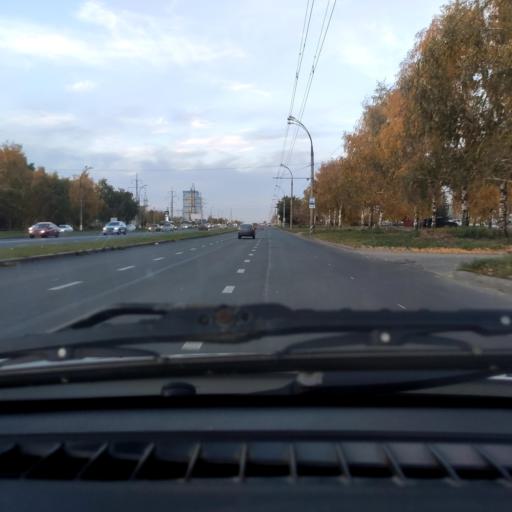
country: RU
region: Samara
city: Tol'yatti
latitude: 53.5434
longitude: 49.2650
